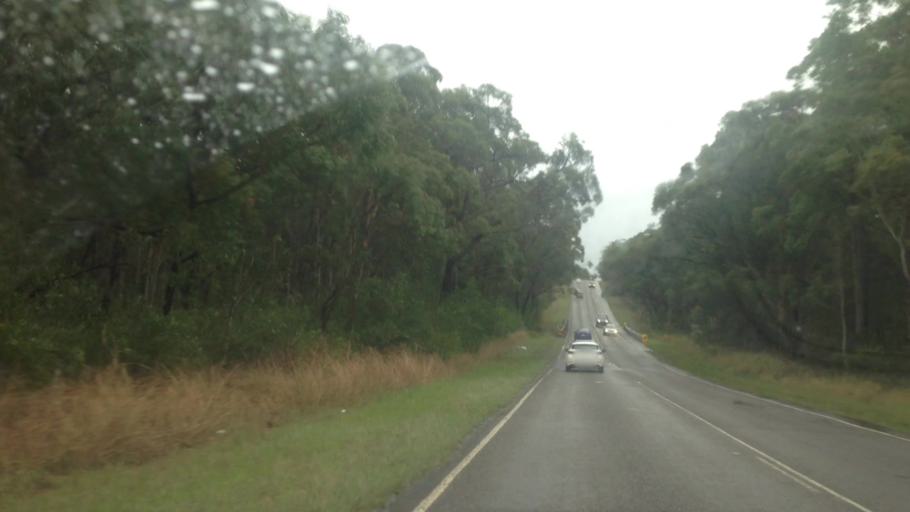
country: AU
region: New South Wales
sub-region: Lake Macquarie Shire
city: Dora Creek
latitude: -33.1472
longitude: 151.4790
